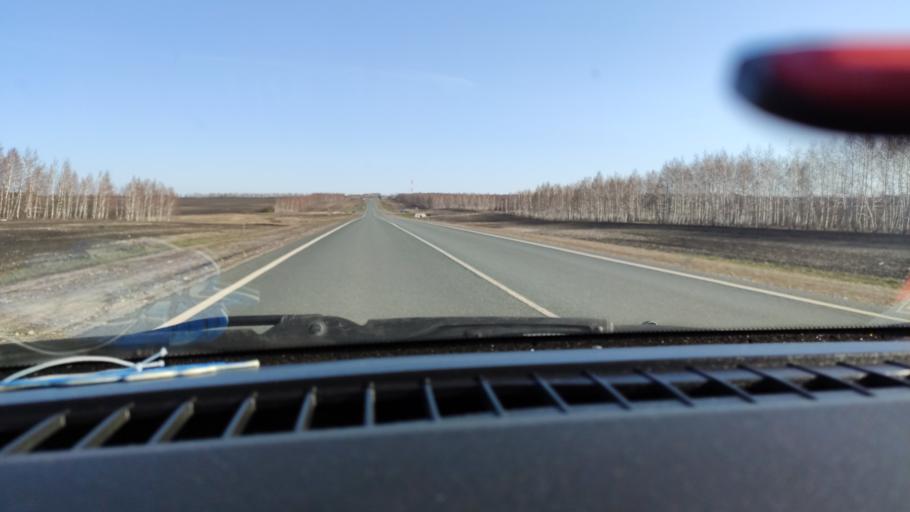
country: RU
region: Samara
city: Syzran'
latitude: 52.9124
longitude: 48.3001
